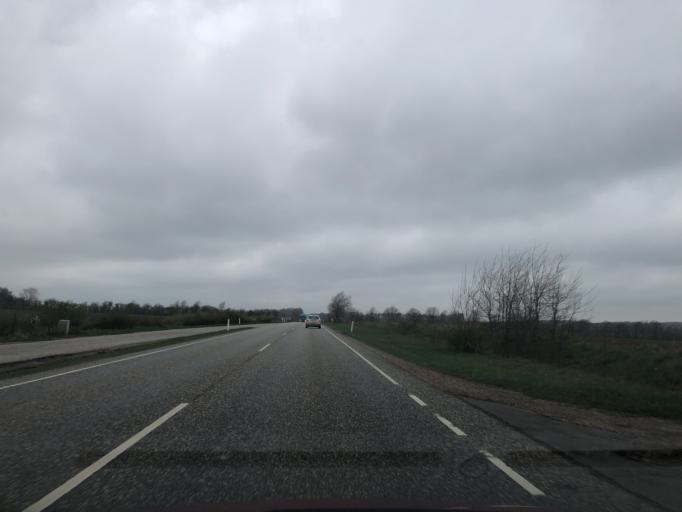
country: DK
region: Central Jutland
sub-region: Holstebro Kommune
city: Holstebro
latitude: 56.3174
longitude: 8.6830
